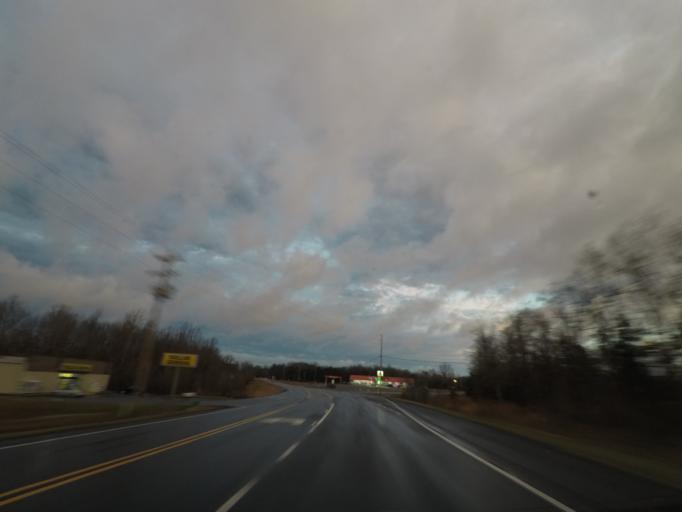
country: US
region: North Carolina
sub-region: Alamance County
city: Mebane
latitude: 36.2446
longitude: -79.1896
